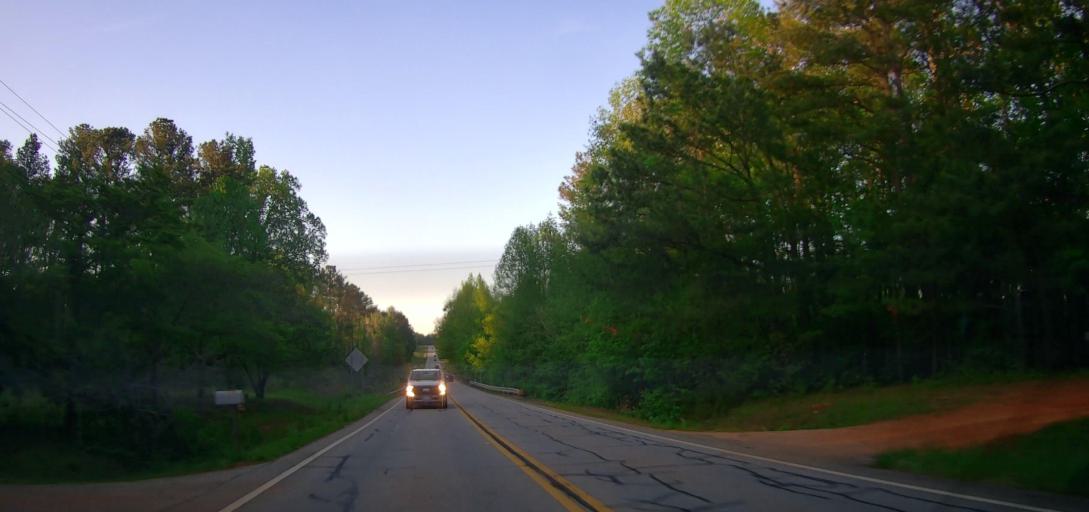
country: US
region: Georgia
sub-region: Newton County
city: Oakwood
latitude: 33.4896
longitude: -83.9554
